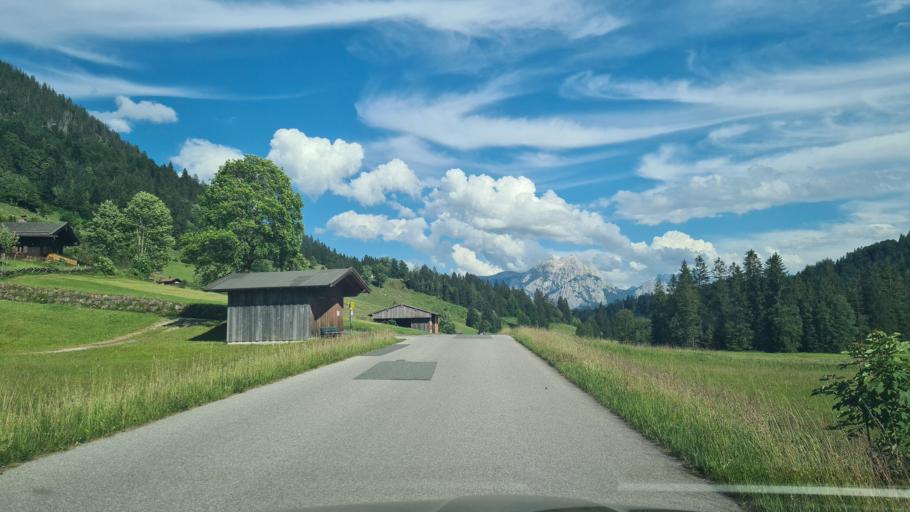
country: AT
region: Salzburg
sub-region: Politischer Bezirk Zell am See
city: Unken
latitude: 47.6606
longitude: 12.6622
